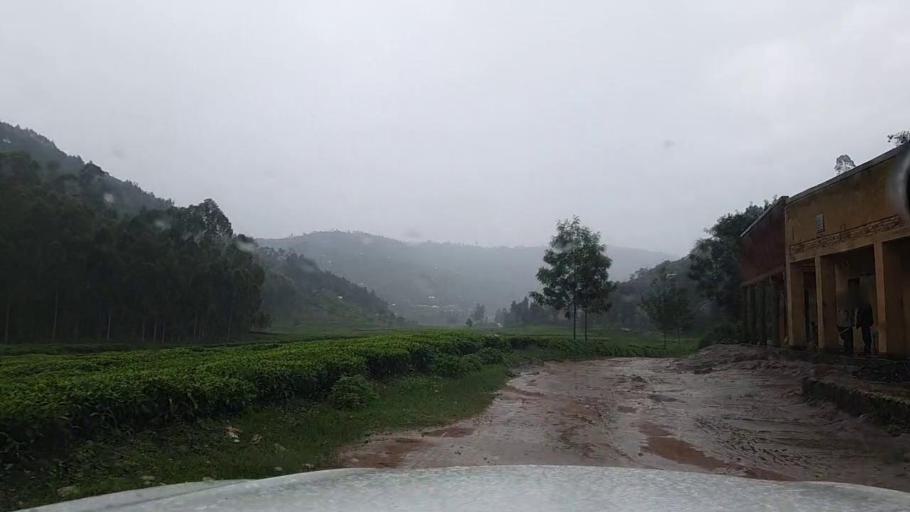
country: RW
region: Northern Province
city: Byumba
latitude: -1.6517
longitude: 29.9189
